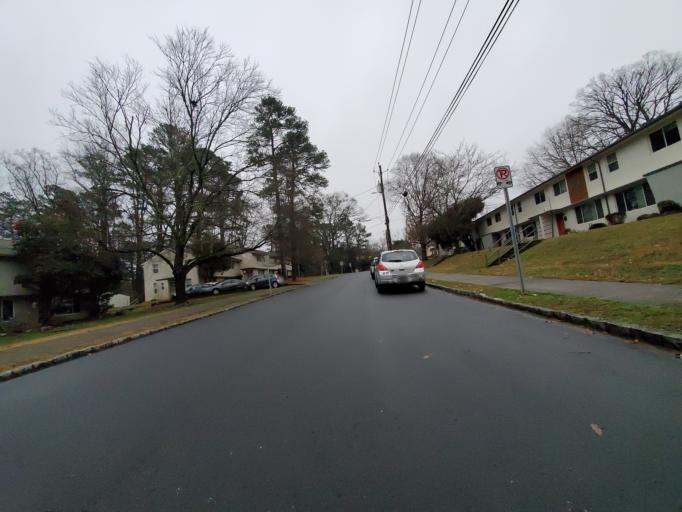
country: US
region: Georgia
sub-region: DeKalb County
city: North Decatur
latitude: 33.7917
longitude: -84.3018
